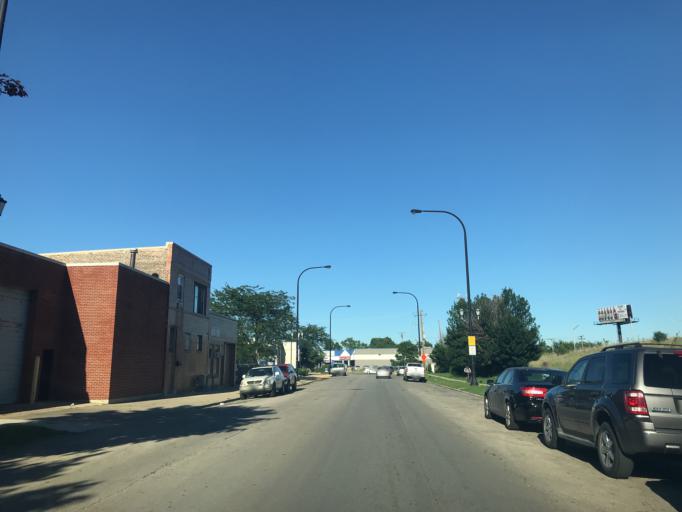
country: US
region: Illinois
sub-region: Cook County
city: Cicero
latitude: 41.8458
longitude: -87.7462
